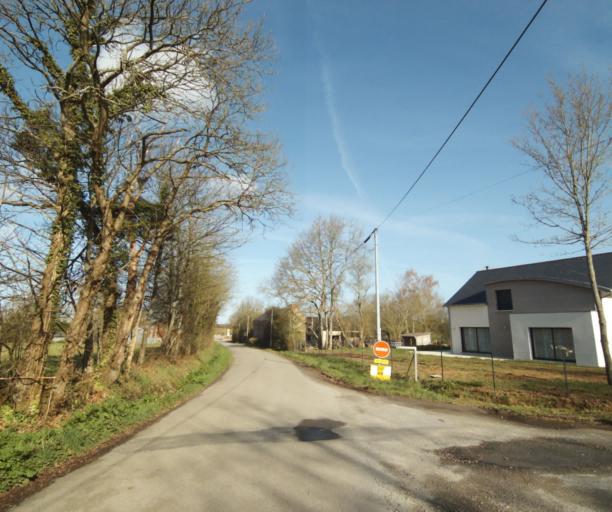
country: FR
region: Pays de la Loire
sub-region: Departement de la Loire-Atlantique
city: Bouvron
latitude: 47.4087
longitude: -1.8411
